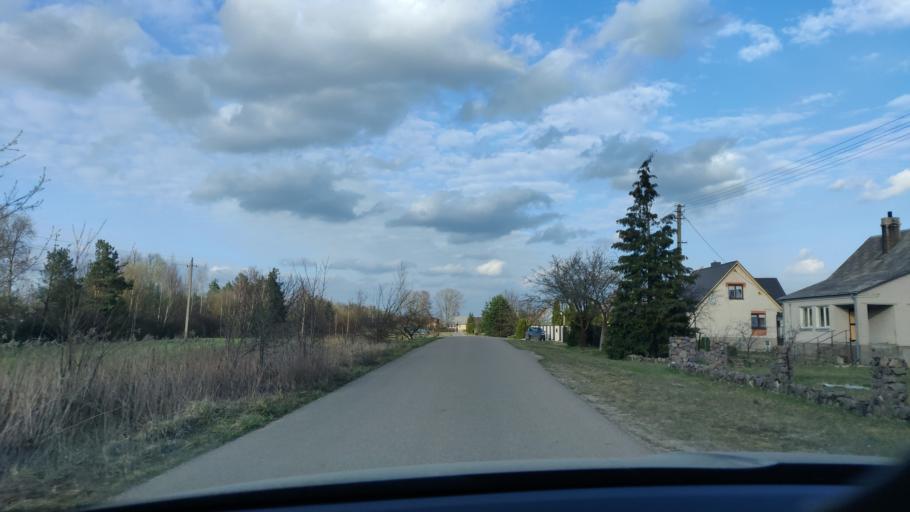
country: LT
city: Trakai
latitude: 54.6075
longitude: 24.9703
